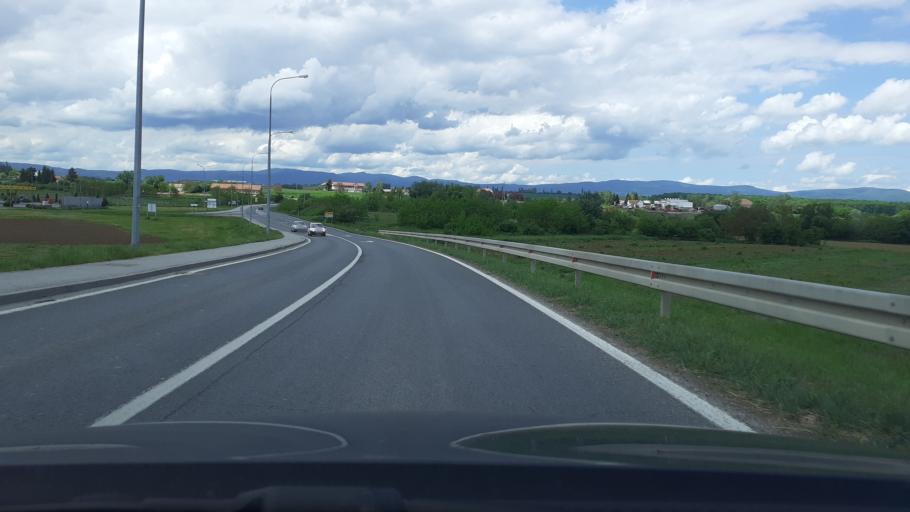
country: HR
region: Pozesko-Slavonska
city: Vidovci
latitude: 45.3365
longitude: 17.7095
